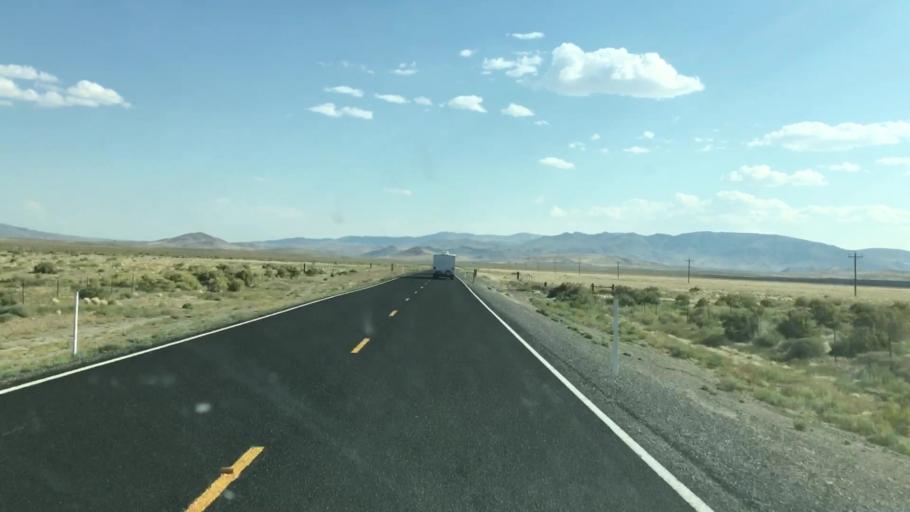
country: US
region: Nevada
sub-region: Lyon County
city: Fernley
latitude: 39.6842
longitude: -119.3349
